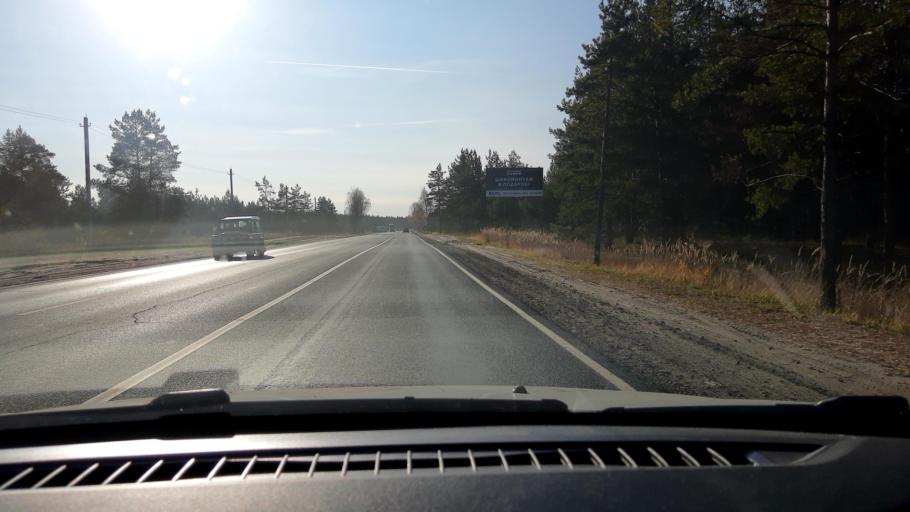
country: RU
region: Nizjnij Novgorod
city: Dzerzhinsk
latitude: 56.2810
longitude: 43.4753
